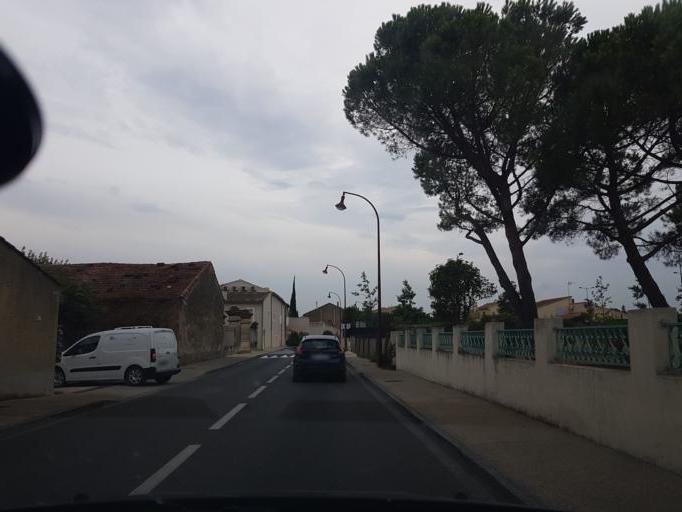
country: FR
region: Provence-Alpes-Cote d'Azur
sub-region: Departement du Vaucluse
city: Entraigues-sur-la-Sorgue
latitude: 44.0046
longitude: 4.9227
